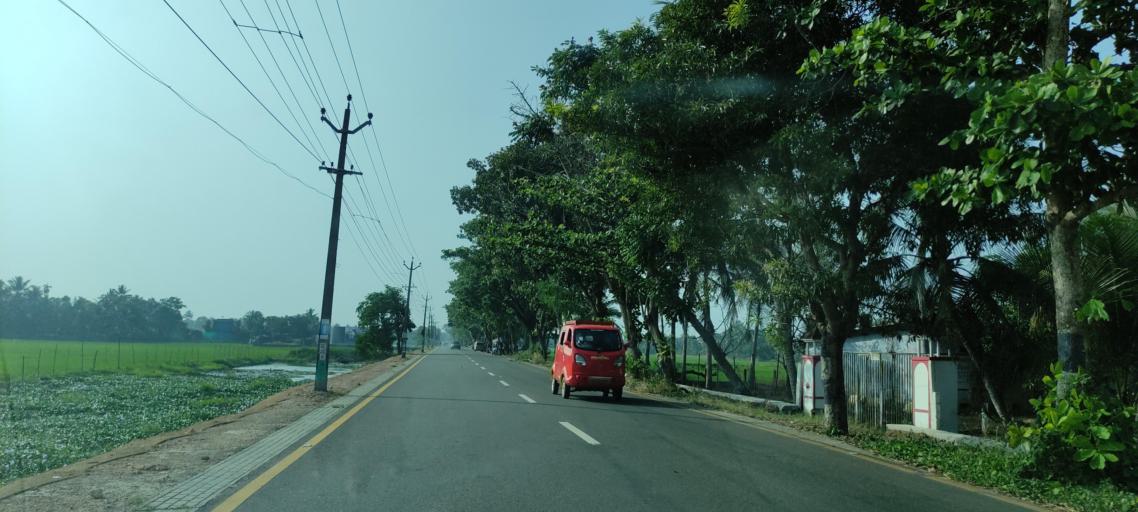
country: IN
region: Kerala
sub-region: Kottayam
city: Changanacheri
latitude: 9.3658
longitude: 76.4374
